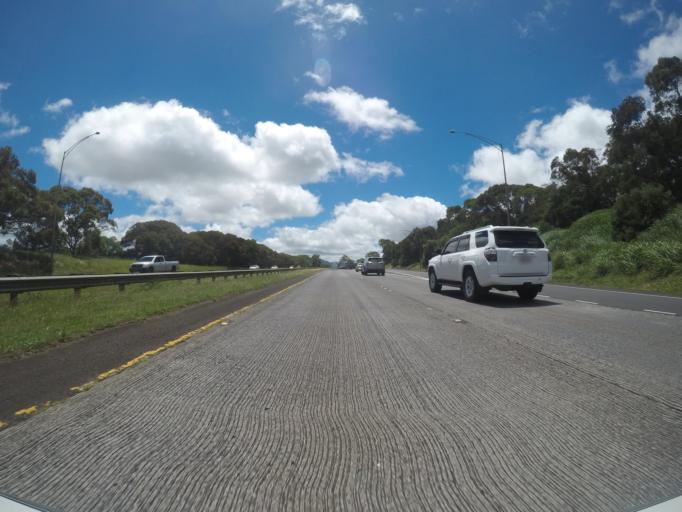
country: US
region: Hawaii
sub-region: Honolulu County
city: Waipi'o Acres
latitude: 21.4758
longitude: -158.0187
